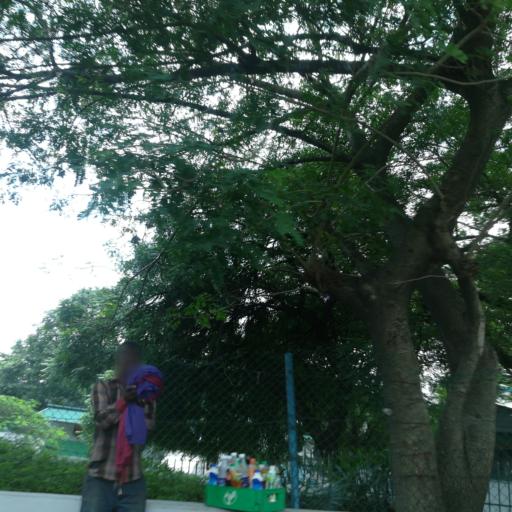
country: NG
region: Lagos
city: Somolu
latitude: 6.5578
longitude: 3.3688
